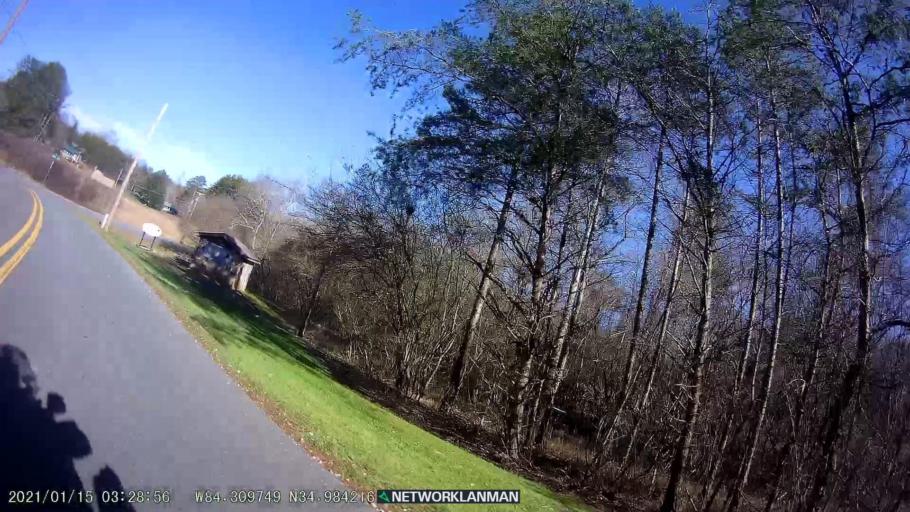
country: US
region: Georgia
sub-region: Fannin County
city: McCaysville
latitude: 34.9844
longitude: -84.3097
